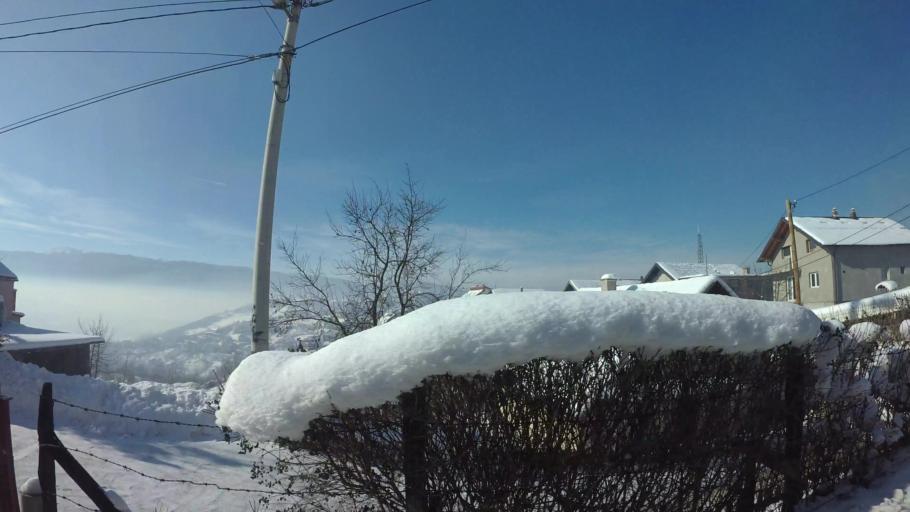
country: BA
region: Federation of Bosnia and Herzegovina
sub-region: Kanton Sarajevo
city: Sarajevo
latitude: 43.8389
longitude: 18.3695
